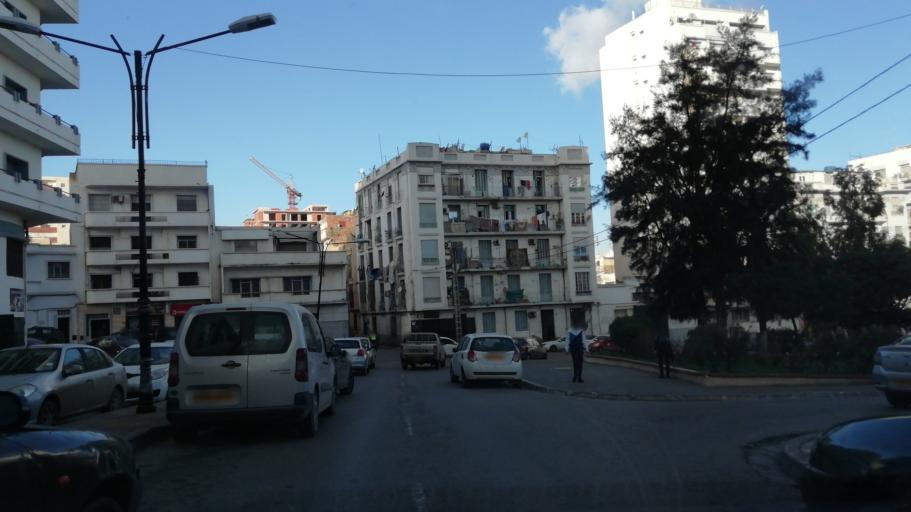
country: DZ
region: Oran
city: Oran
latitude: 35.7038
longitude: -0.6306
